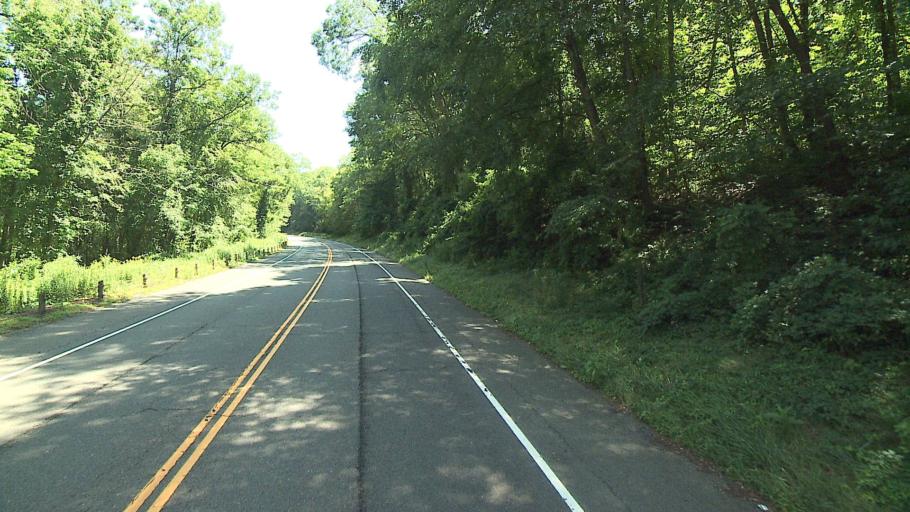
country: US
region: Connecticut
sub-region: Hartford County
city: Collinsville
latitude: 41.7780
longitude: -72.9196
